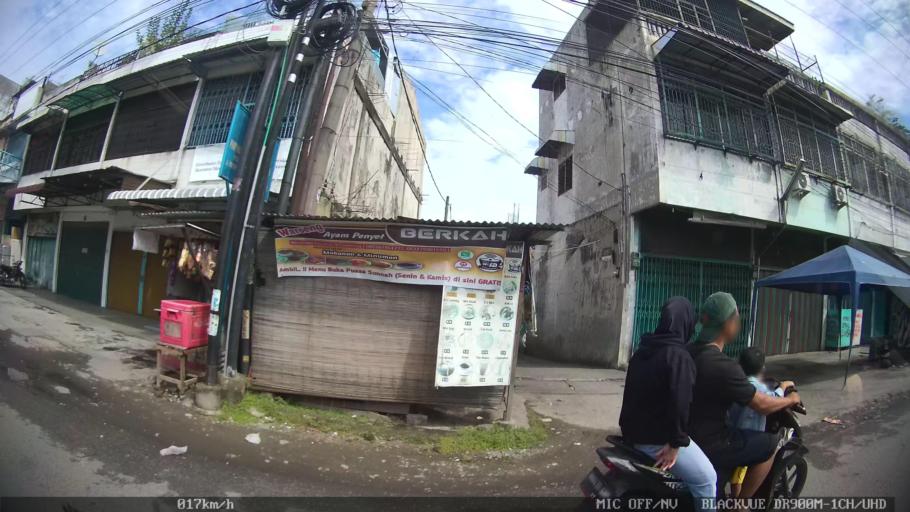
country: ID
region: North Sumatra
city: Medan
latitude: 3.6273
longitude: 98.6672
